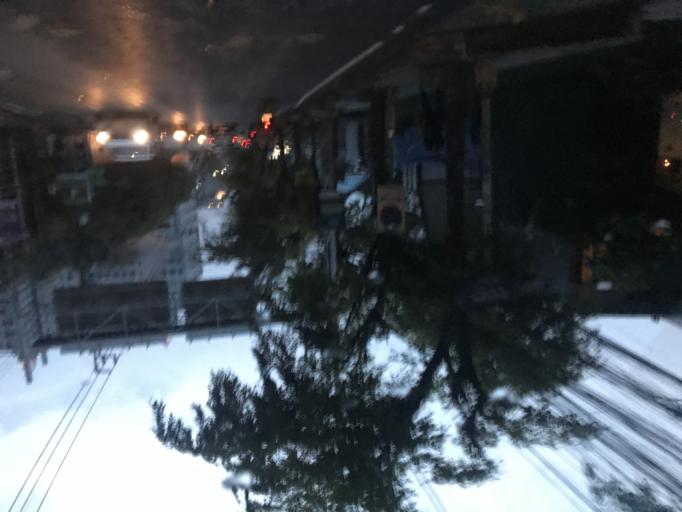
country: TH
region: Bangkok
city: Phra Khanong
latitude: 13.7051
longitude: 100.5968
